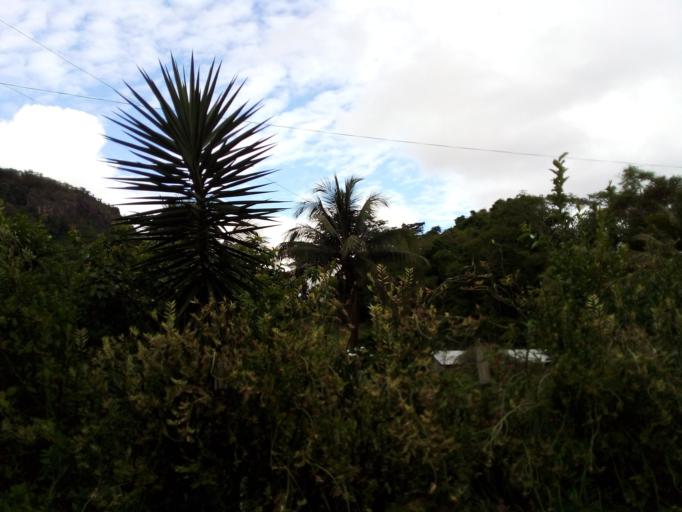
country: BR
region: Espirito Santo
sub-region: Joao Neiva
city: Joao Neiva
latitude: -19.7513
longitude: -40.3666
